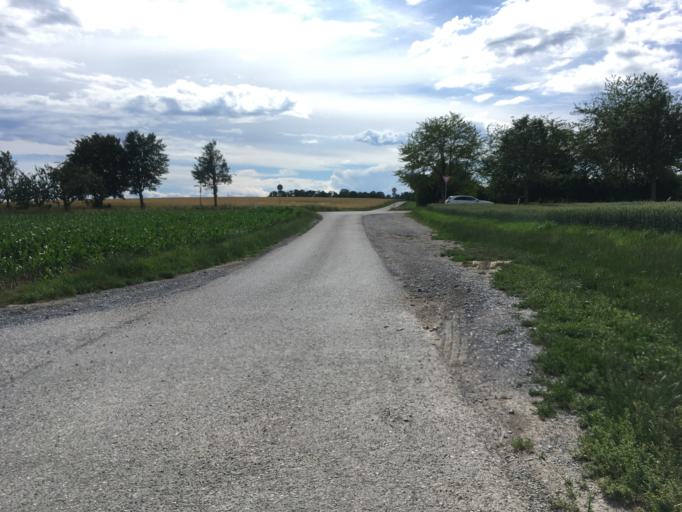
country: DE
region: Baden-Wuerttemberg
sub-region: Regierungsbezirk Stuttgart
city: Oberriexingen
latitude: 48.9420
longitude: 9.0224
